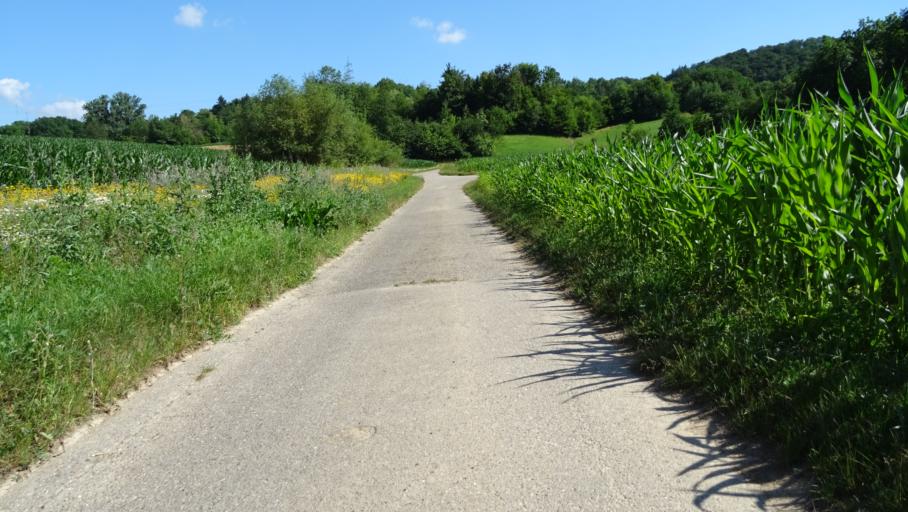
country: DE
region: Baden-Wuerttemberg
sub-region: Karlsruhe Region
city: Binau
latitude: 49.3646
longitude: 9.0683
